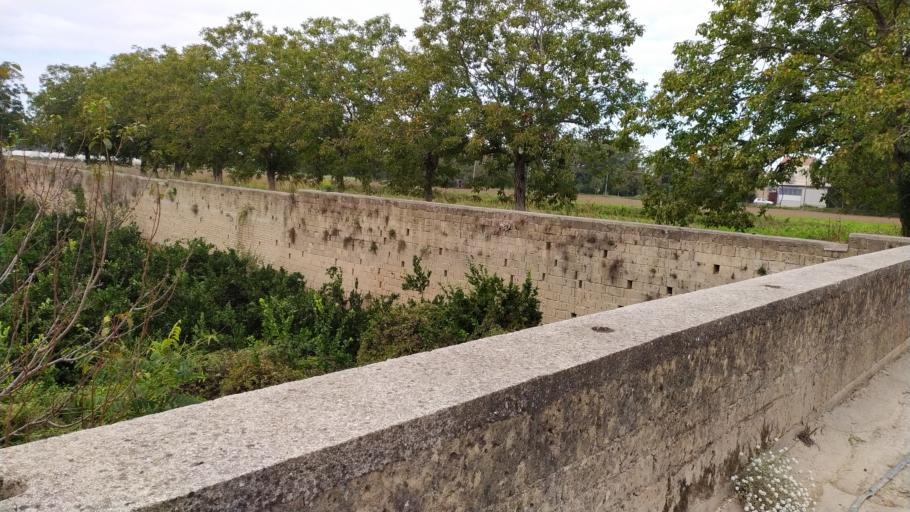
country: IT
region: Campania
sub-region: Provincia di Caserta
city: Montedecoro
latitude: 41.0166
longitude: 14.4059
